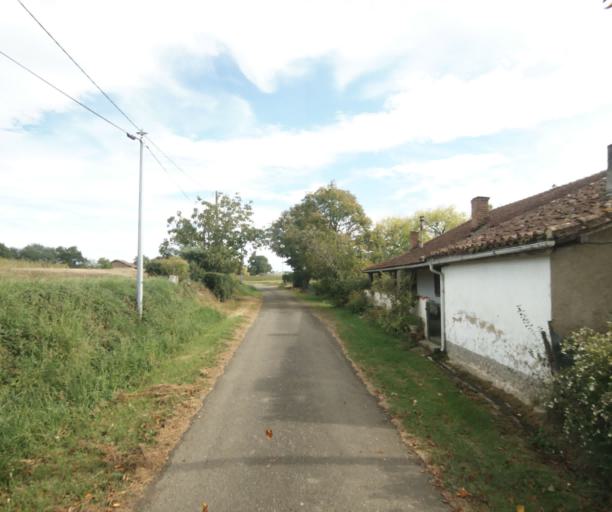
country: FR
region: Midi-Pyrenees
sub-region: Departement du Gers
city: Cazaubon
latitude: 43.8800
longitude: -0.1487
